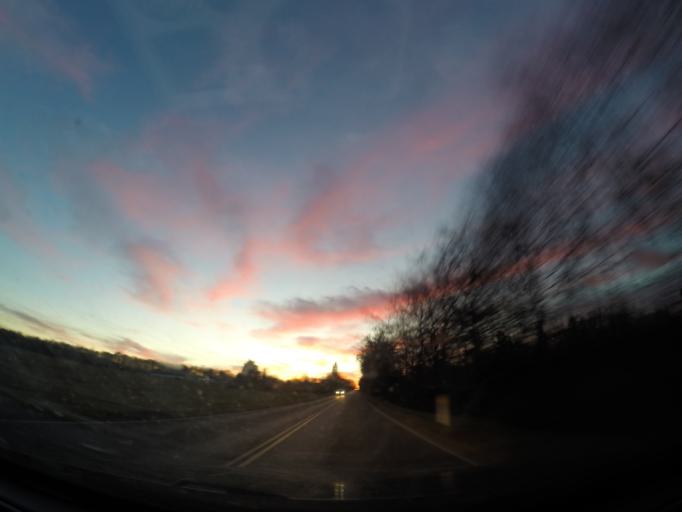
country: DK
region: Capital Region
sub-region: Hoje-Taastrup Kommune
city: Taastrup
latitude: 55.6677
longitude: 12.2844
